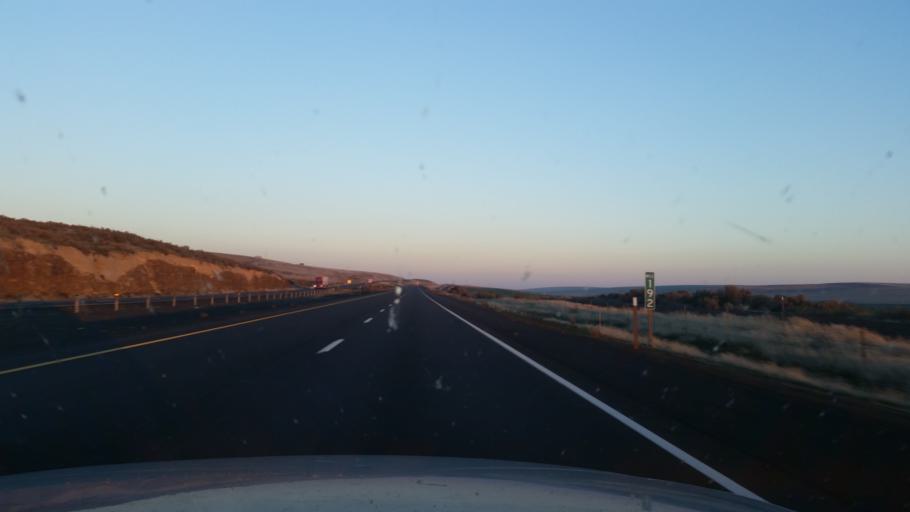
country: US
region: Washington
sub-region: Grant County
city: Warden
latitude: 47.0842
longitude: -118.9796
